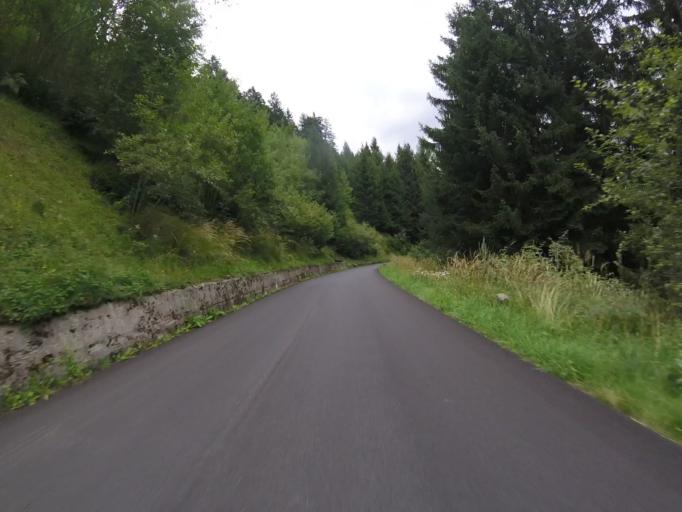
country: IT
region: Lombardy
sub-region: Provincia di Brescia
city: Monno
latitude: 46.2244
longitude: 10.3260
